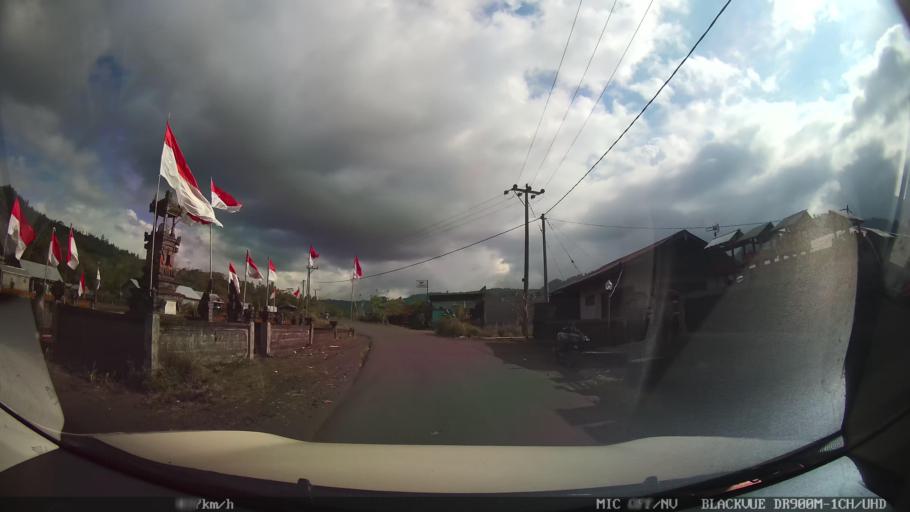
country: ID
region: Bali
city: Banjar Kedisan
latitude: -8.2250
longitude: 115.3598
